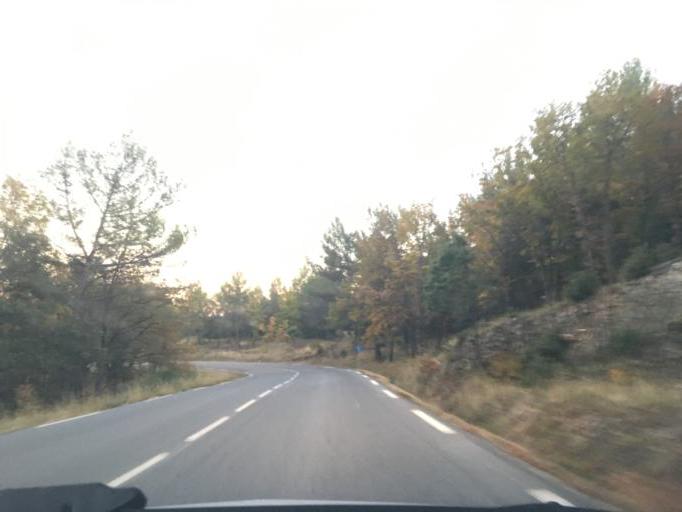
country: FR
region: Provence-Alpes-Cote d'Azur
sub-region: Departement du Var
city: Montferrat
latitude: 43.6318
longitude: 6.4882
